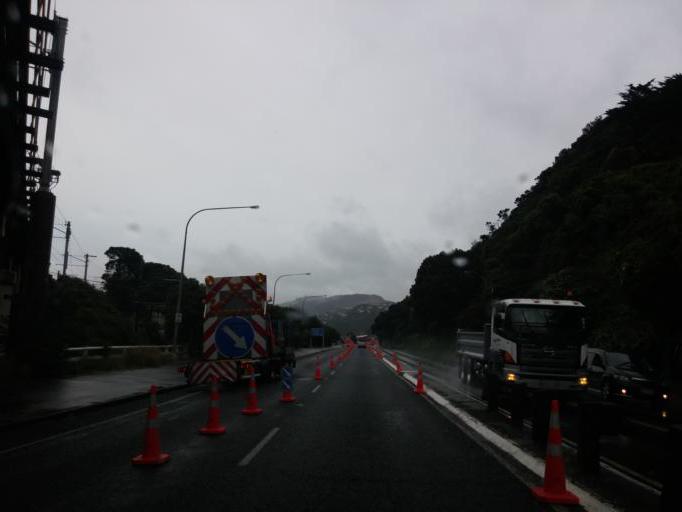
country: NZ
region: Wellington
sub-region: Wellington City
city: Wellington
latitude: -41.2529
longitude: 174.8042
